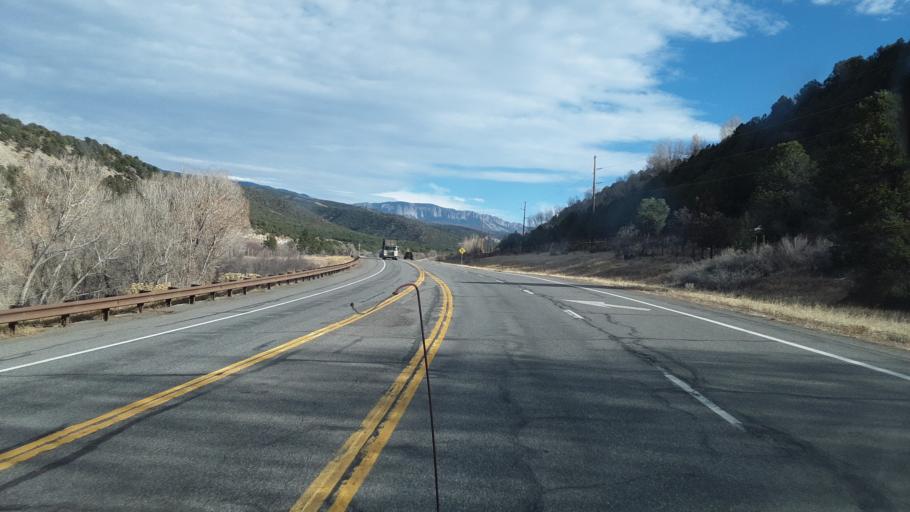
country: US
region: Colorado
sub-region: Ouray County
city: Ouray
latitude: 38.2447
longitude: -107.7567
